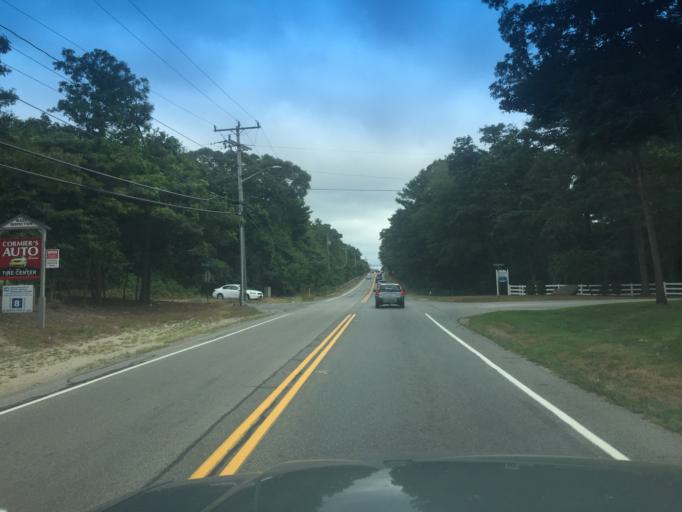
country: US
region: Massachusetts
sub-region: Barnstable County
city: Mashpee
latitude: 41.6162
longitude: -70.5151
